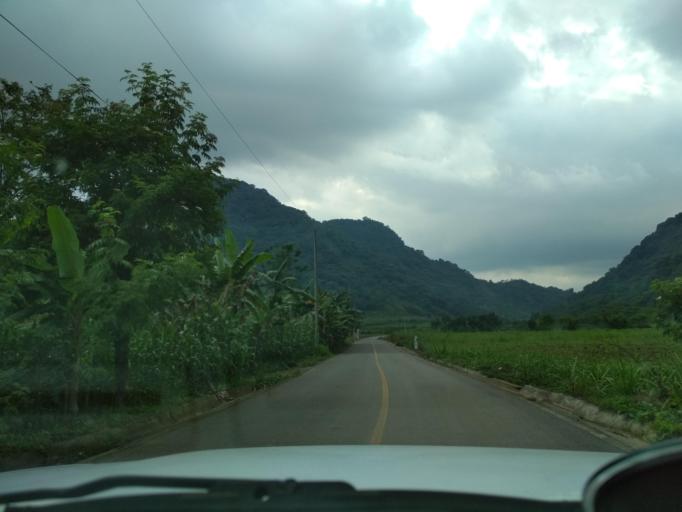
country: MX
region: Veracruz
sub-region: Fortin
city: Santa Lucia Potrerillo
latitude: 18.9487
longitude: -97.0600
